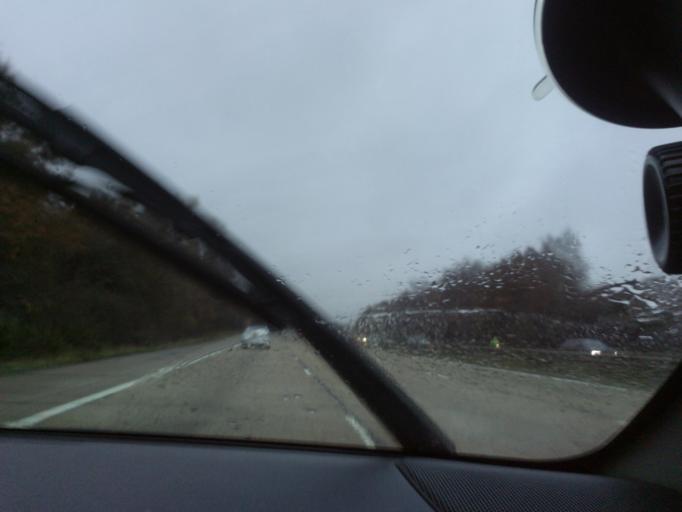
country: GB
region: England
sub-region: Hampshire
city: West End
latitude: 50.9353
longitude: -1.3378
